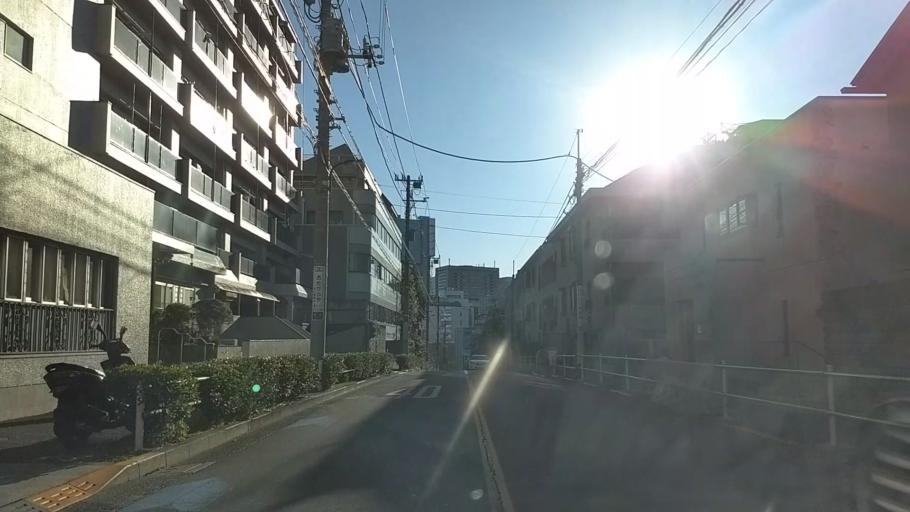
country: JP
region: Tokyo
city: Tokyo
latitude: 35.6353
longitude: 139.7347
